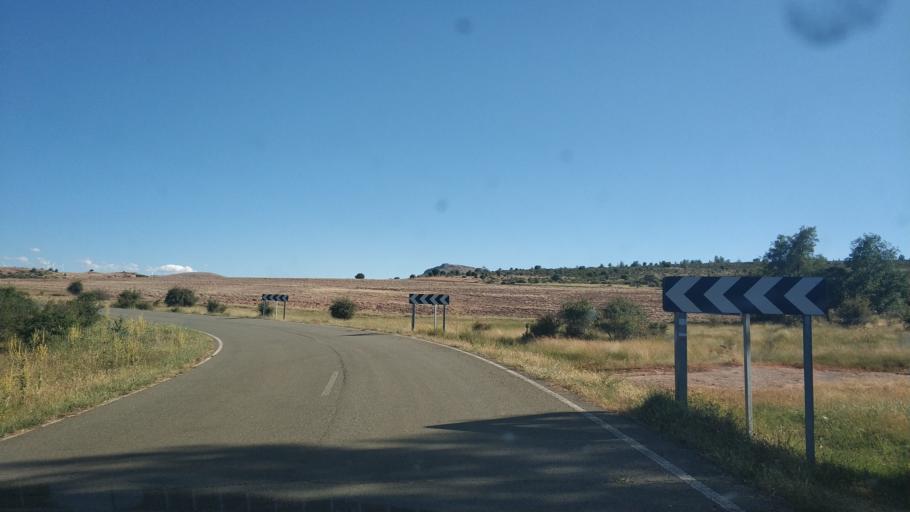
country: ES
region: Castille and Leon
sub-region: Provincia de Soria
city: Montejo de Tiermes
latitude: 41.3359
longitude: -3.1526
